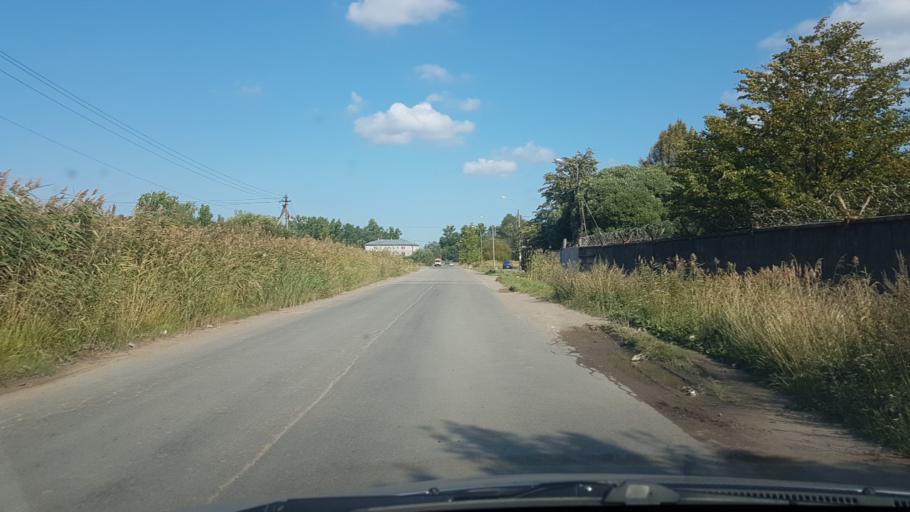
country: RU
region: St.-Petersburg
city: Sosnovaya Polyana
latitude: 59.8435
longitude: 30.1195
